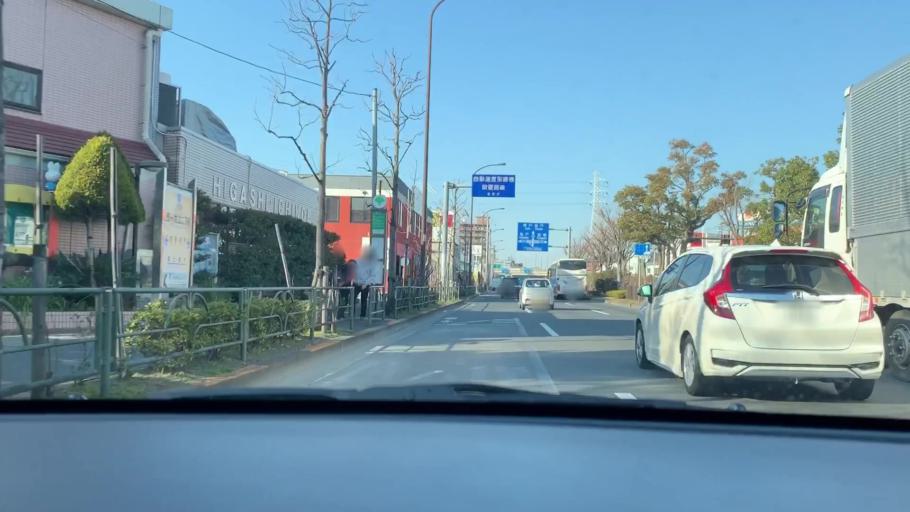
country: JP
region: Tokyo
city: Urayasu
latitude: 35.6982
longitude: 139.8818
